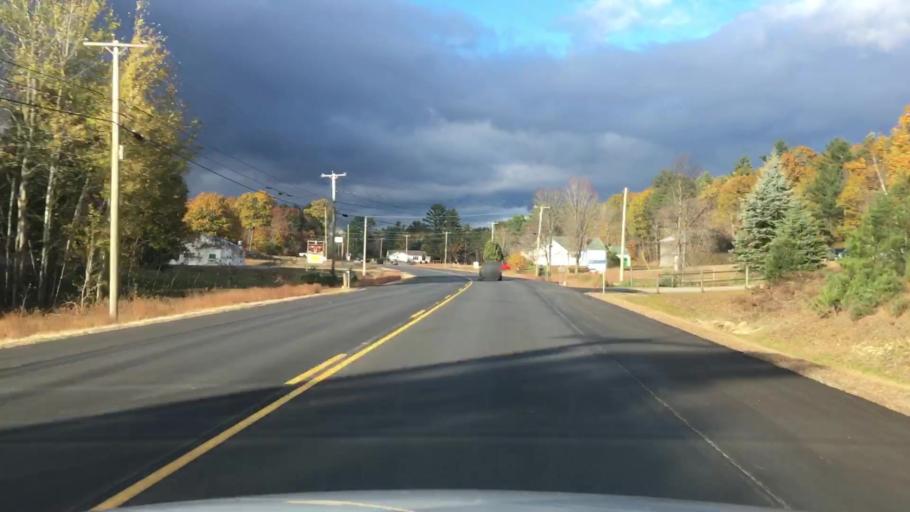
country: US
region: Maine
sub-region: Androscoggin County
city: Livermore
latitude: 44.3646
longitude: -70.2523
